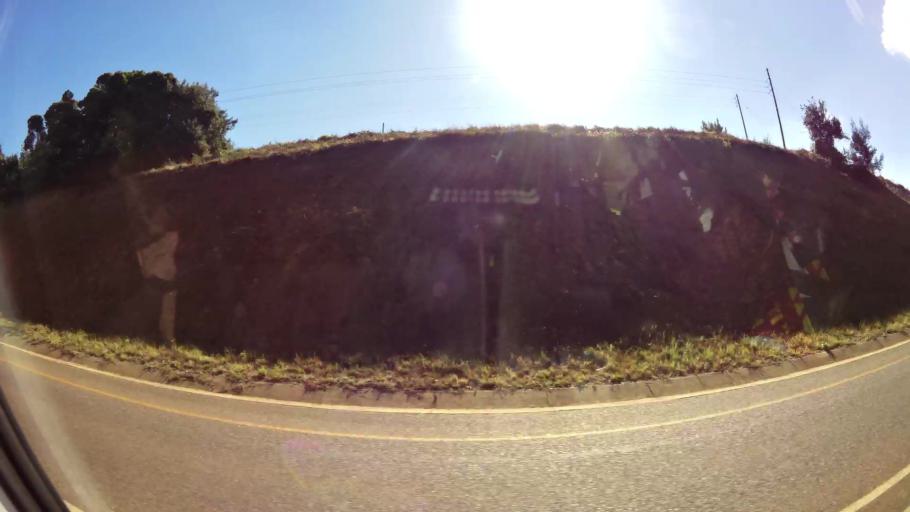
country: ZA
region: Limpopo
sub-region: Capricorn District Municipality
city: Mankoeng
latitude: -23.9184
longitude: 29.9593
